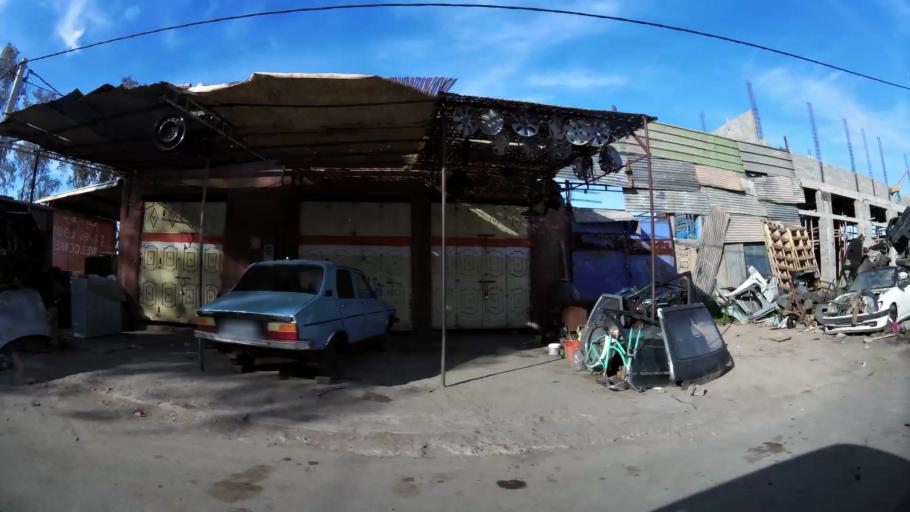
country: MA
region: Marrakech-Tensift-Al Haouz
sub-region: Marrakech
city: Marrakesh
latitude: 31.6807
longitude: -8.0530
